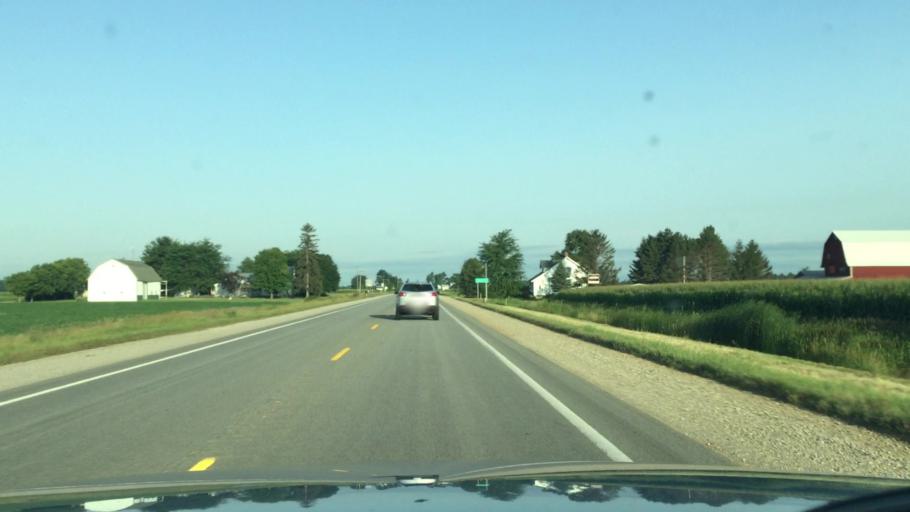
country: US
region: Michigan
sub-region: Montcalm County
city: Carson City
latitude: 43.1763
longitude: -84.7542
